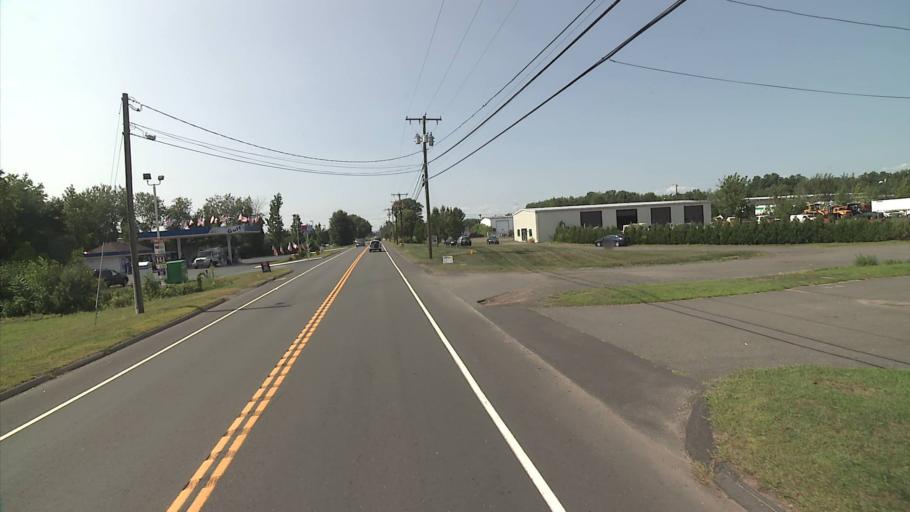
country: US
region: Connecticut
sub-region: Hartford County
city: South Windsor
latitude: 41.8510
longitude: -72.5788
